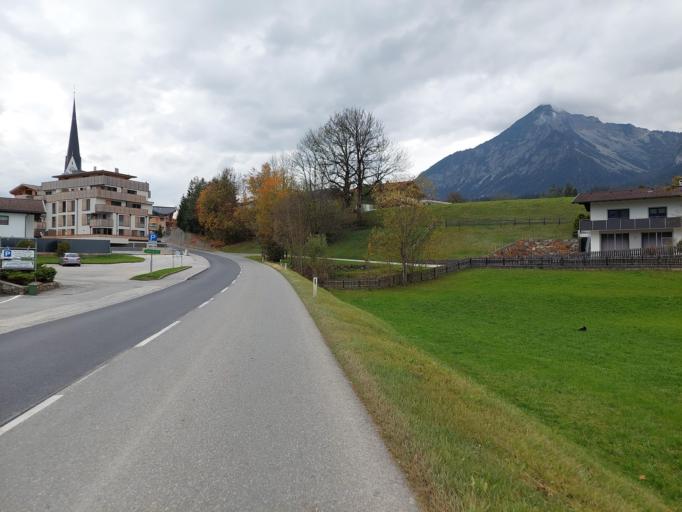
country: AT
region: Tyrol
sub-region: Politischer Bezirk Kufstein
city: Munster
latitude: 47.4226
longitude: 11.8359
